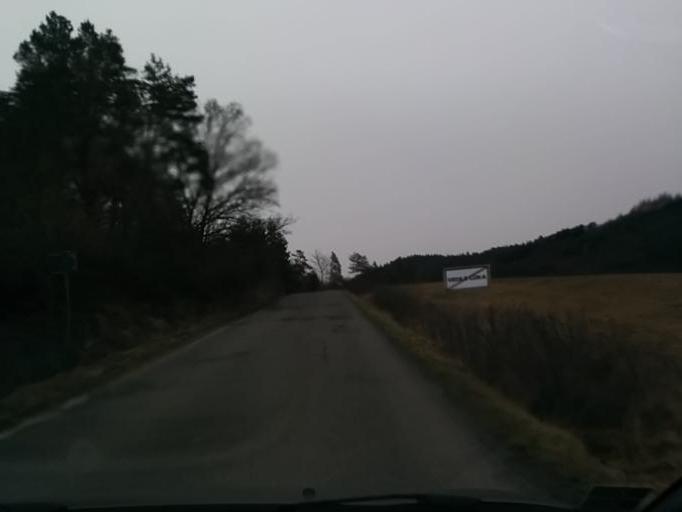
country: SK
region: Banskobystricky
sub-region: Okres Banska Bystrica
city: Zvolen
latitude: 48.6339
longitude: 19.1770
